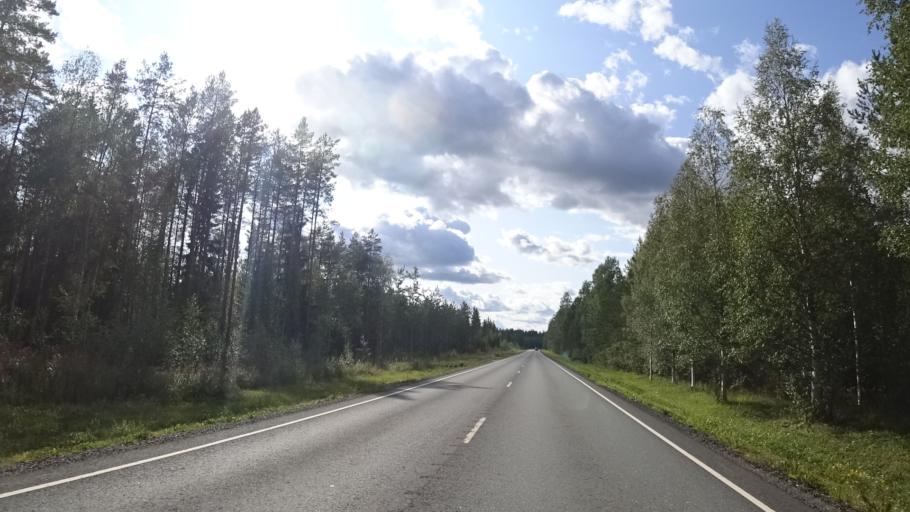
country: RU
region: Republic of Karelia
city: Vyartsilya
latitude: 62.1759
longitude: 30.5622
